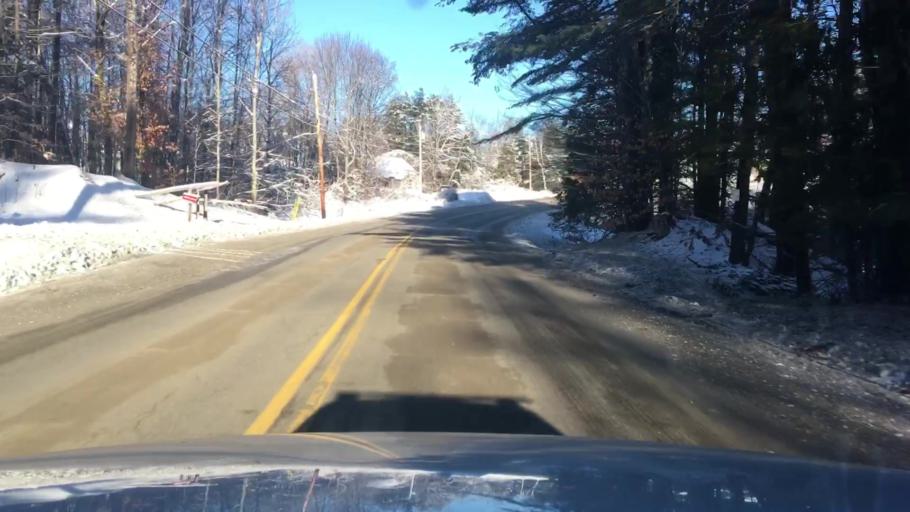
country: US
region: Maine
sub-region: Kennebec County
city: Readfield
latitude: 44.4335
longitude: -69.9656
